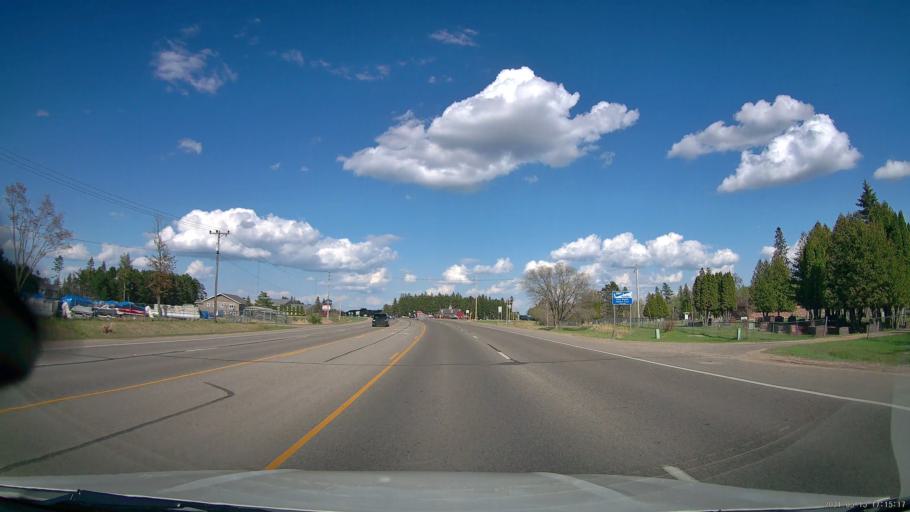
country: US
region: Minnesota
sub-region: Hubbard County
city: Park Rapids
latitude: 46.9219
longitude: -95.0299
